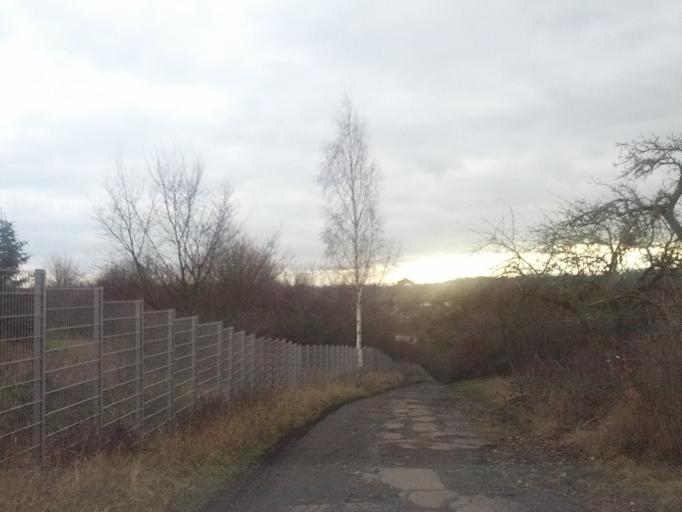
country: DE
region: Thuringia
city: Erfurt
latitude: 50.9674
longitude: 10.9817
